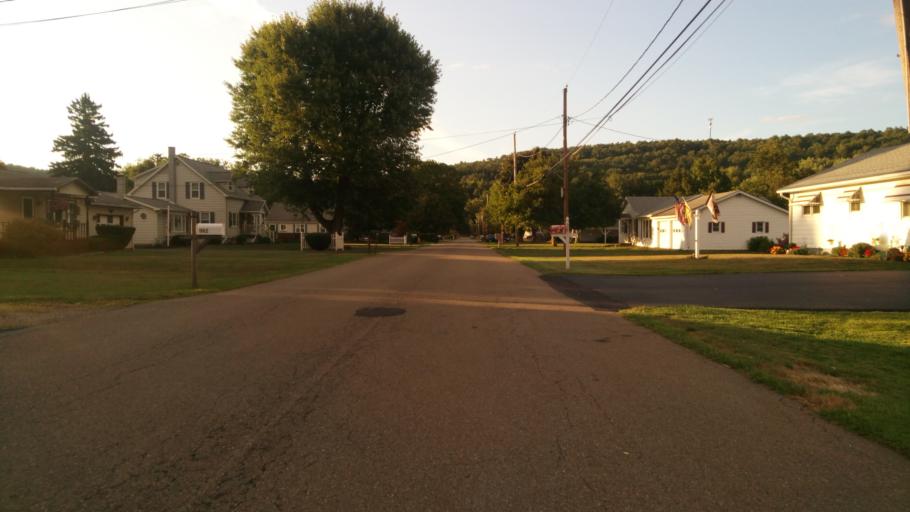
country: US
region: New York
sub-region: Chemung County
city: Southport
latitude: 42.0544
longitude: -76.8281
